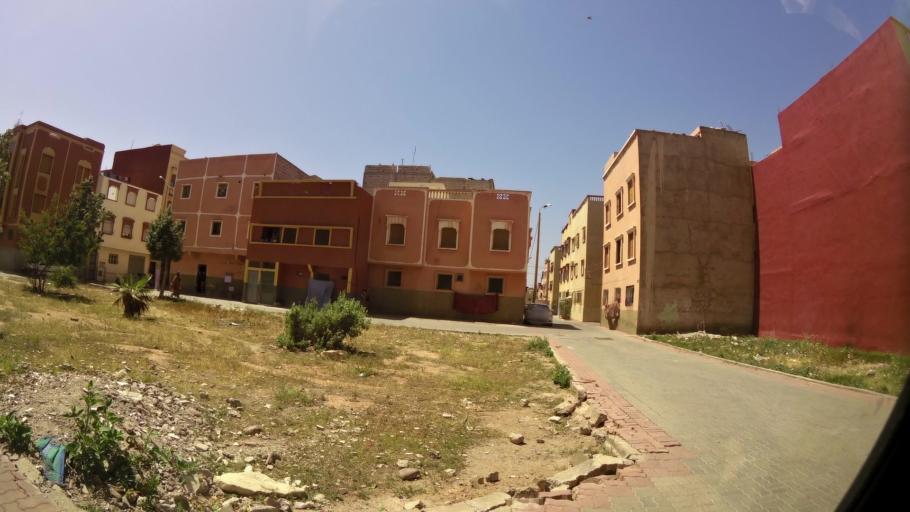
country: MA
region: Souss-Massa-Draa
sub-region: Inezgane-Ait Mellou
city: Inezgane
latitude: 30.3489
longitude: -9.4888
